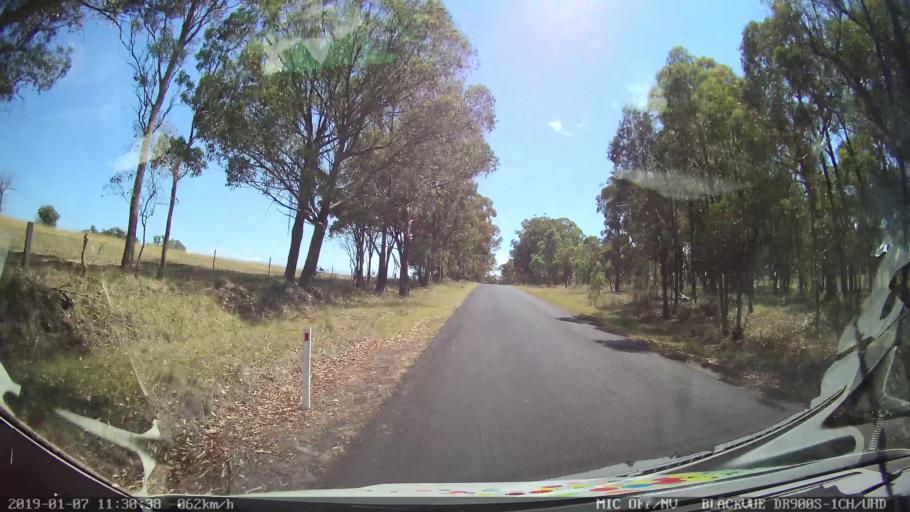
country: AU
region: New South Wales
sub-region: Armidale Dumaresq
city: Armidale
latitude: -30.4274
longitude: 151.5632
